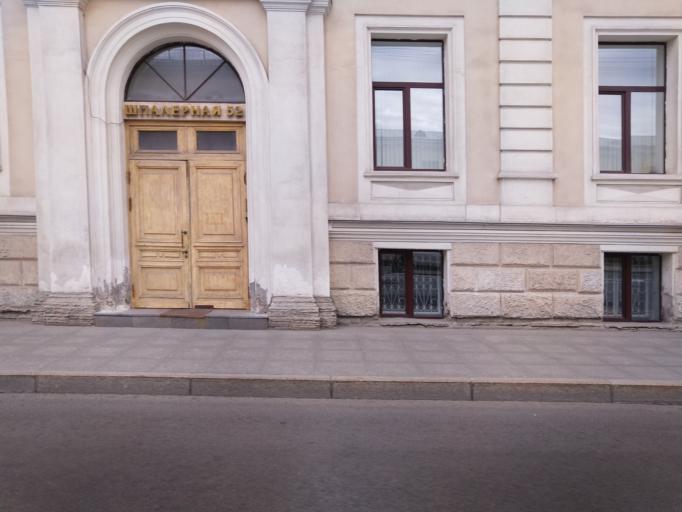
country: RU
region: Leningrad
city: Finlyandskiy
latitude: 59.9488
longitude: 30.3726
